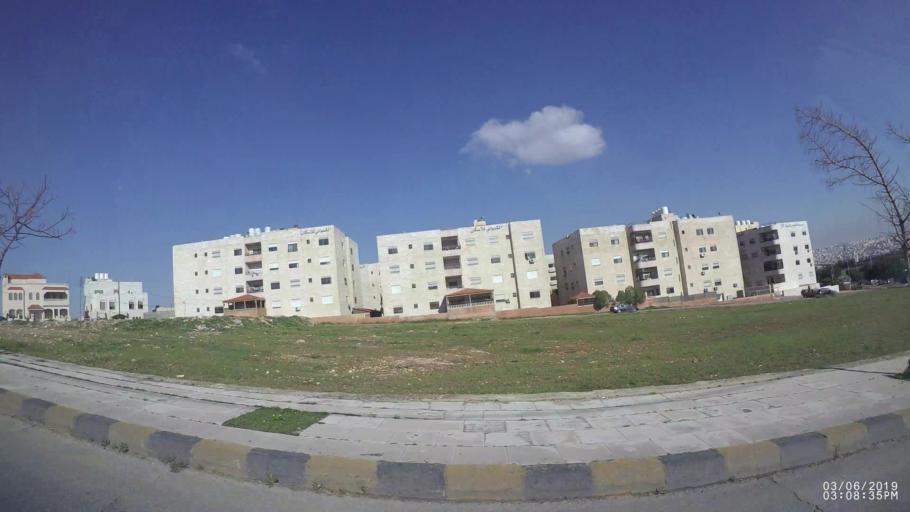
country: JO
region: Amman
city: Amman
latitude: 31.9734
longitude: 35.9360
